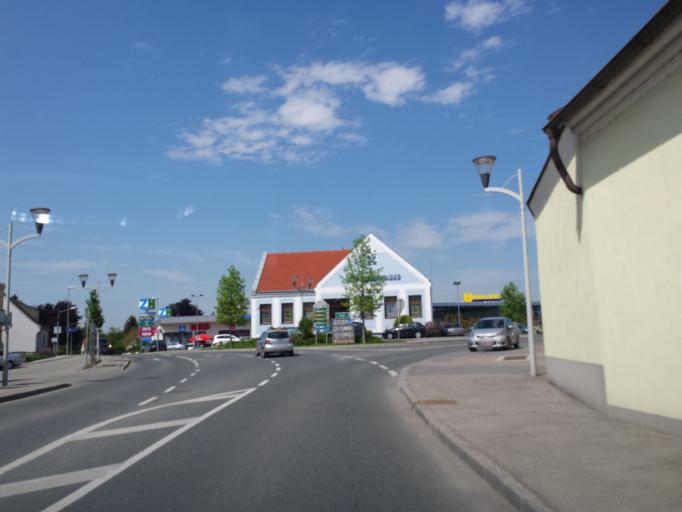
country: AT
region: Lower Austria
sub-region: Politischer Bezirk Tulln
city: Atzenbrugg
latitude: 48.3001
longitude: 15.8937
